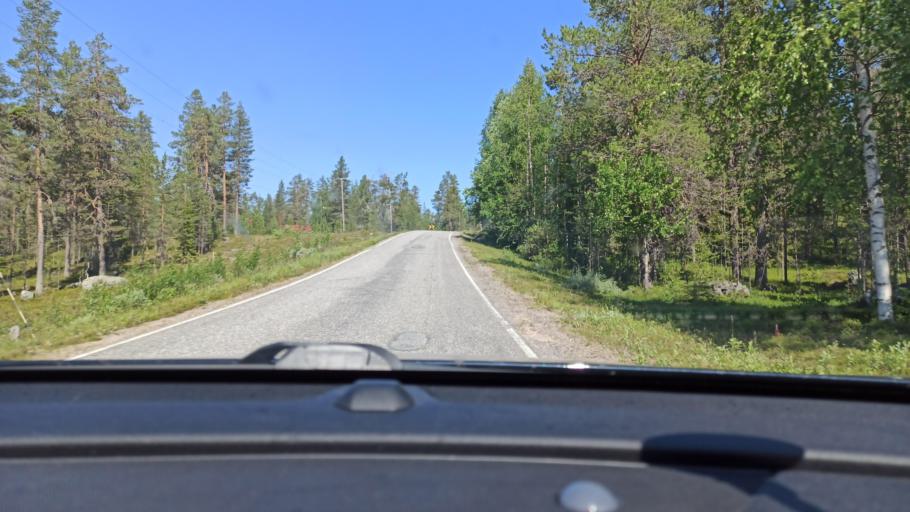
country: FI
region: Lapland
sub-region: Tunturi-Lappi
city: Kolari
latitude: 67.6361
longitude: 24.1576
